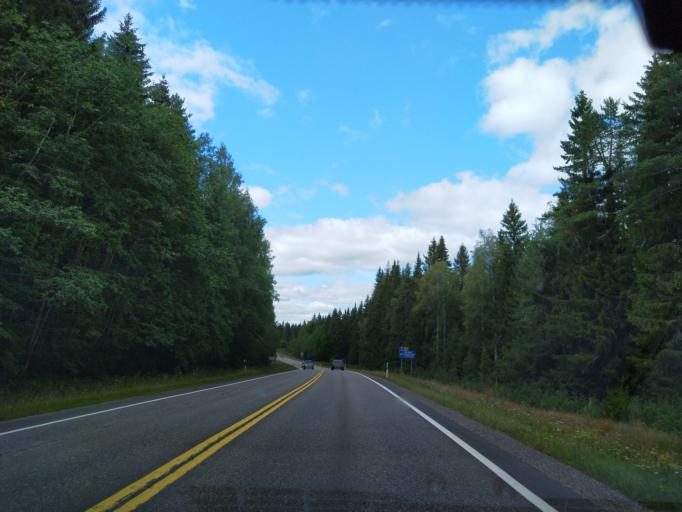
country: FI
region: Haeme
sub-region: Haemeenlinna
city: Renko
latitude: 60.7602
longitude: 24.2901
